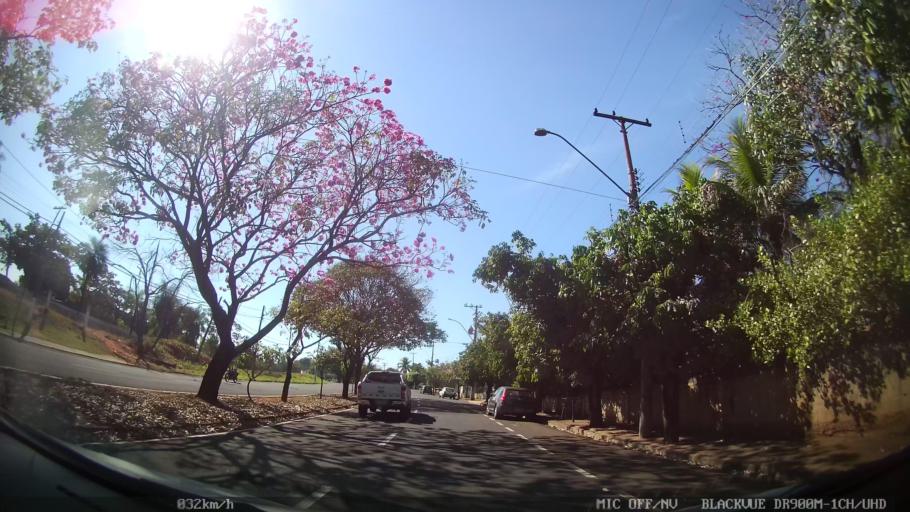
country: BR
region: Sao Paulo
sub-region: Sao Jose Do Rio Preto
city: Sao Jose do Rio Preto
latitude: -20.8147
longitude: -49.4320
